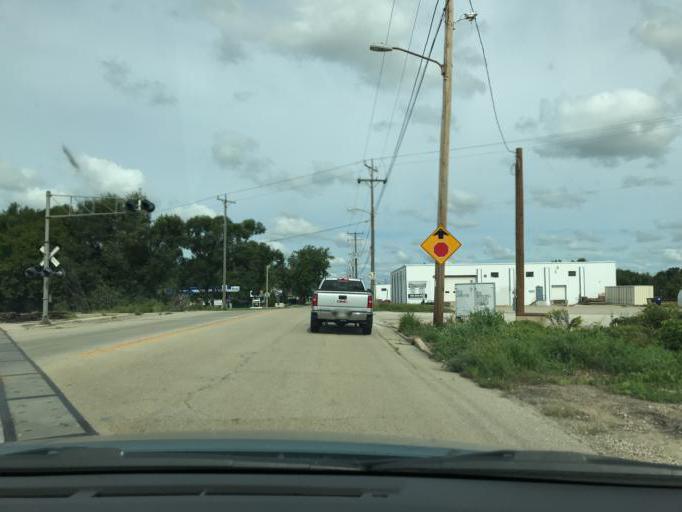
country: US
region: Wisconsin
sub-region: Racine County
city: Burlington
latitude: 42.6677
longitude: -88.2664
